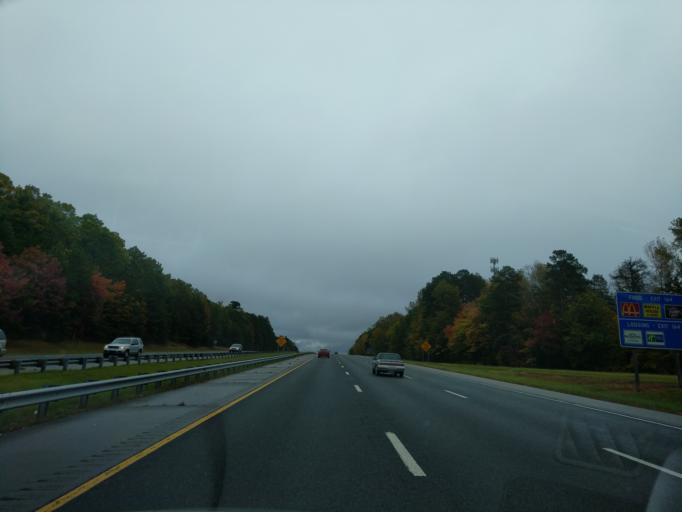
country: US
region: North Carolina
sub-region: Orange County
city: Hillsborough
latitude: 36.0591
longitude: -79.1236
